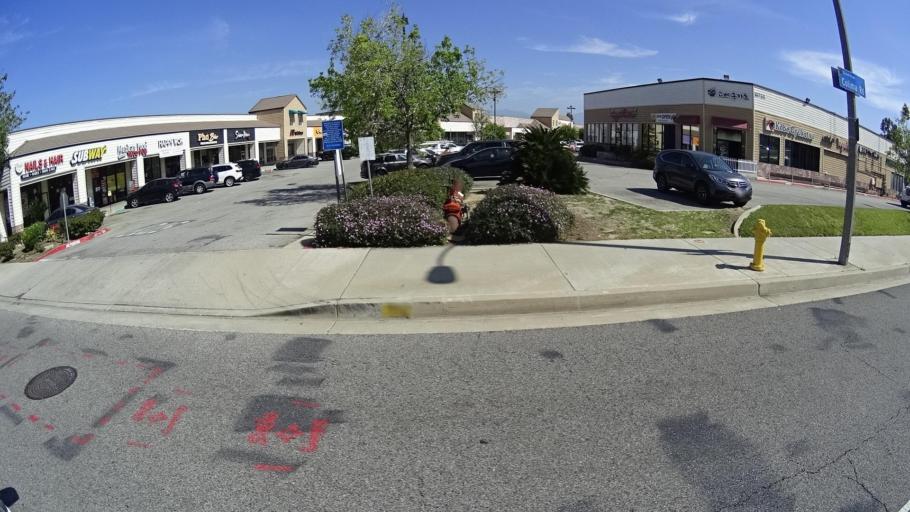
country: US
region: California
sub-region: Los Angeles County
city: Rowland Heights
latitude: 33.9862
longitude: -117.8725
